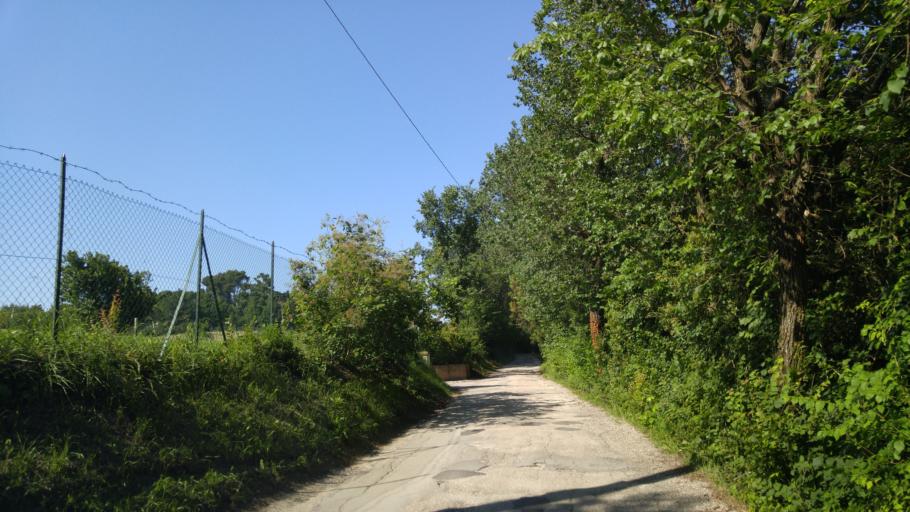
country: IT
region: The Marches
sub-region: Provincia di Pesaro e Urbino
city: Centinarola
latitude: 43.8474
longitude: 12.9915
